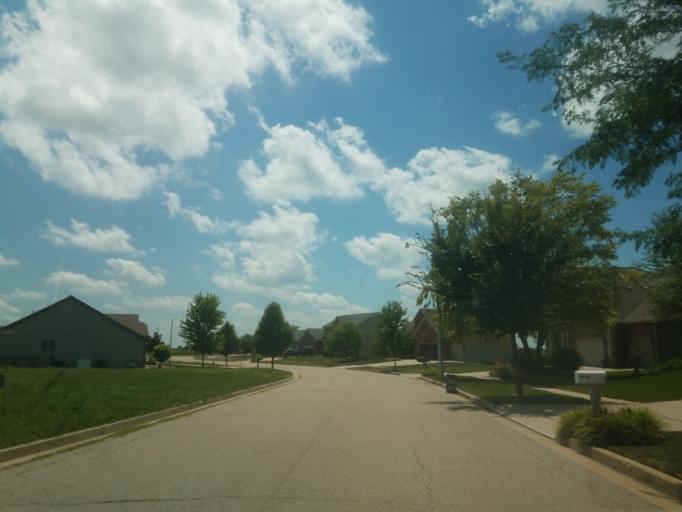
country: US
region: Illinois
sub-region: McLean County
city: Bloomington
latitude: 40.4443
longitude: -89.0351
